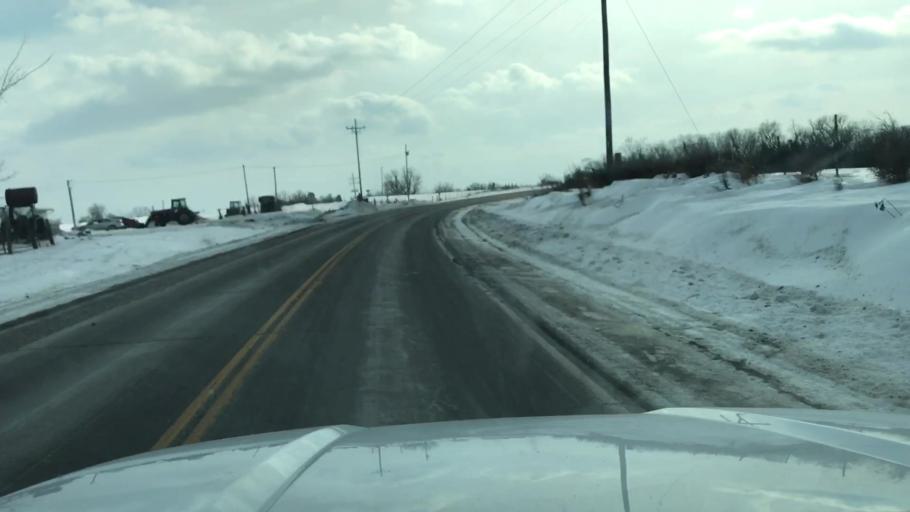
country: US
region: Missouri
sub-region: Gentry County
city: Stanberry
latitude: 40.3695
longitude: -94.6474
